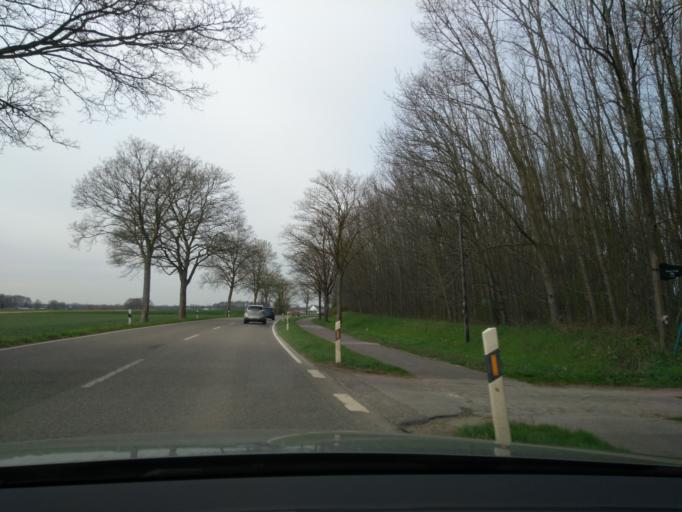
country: DE
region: North Rhine-Westphalia
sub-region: Regierungsbezirk Dusseldorf
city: Sonsbeck
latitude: 51.5932
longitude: 6.3999
